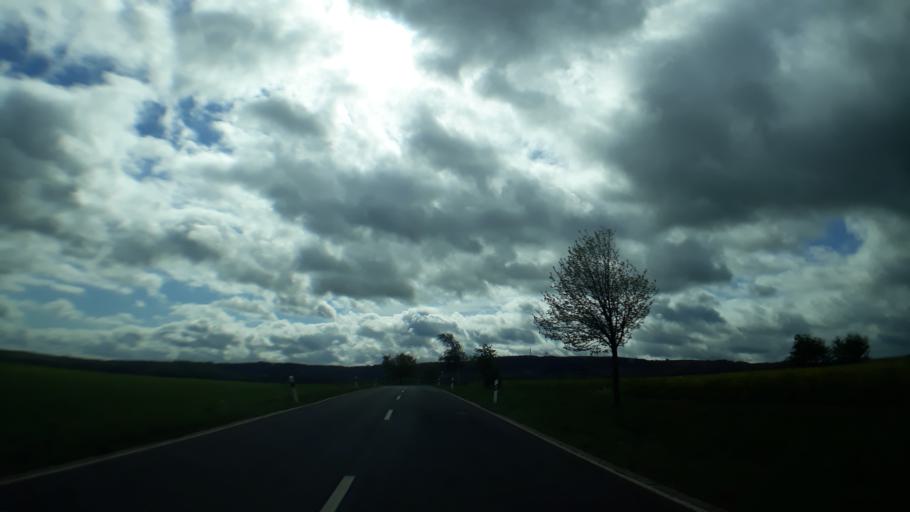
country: DE
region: North Rhine-Westphalia
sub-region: Regierungsbezirk Koln
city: Kall
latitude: 50.5810
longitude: 6.5934
